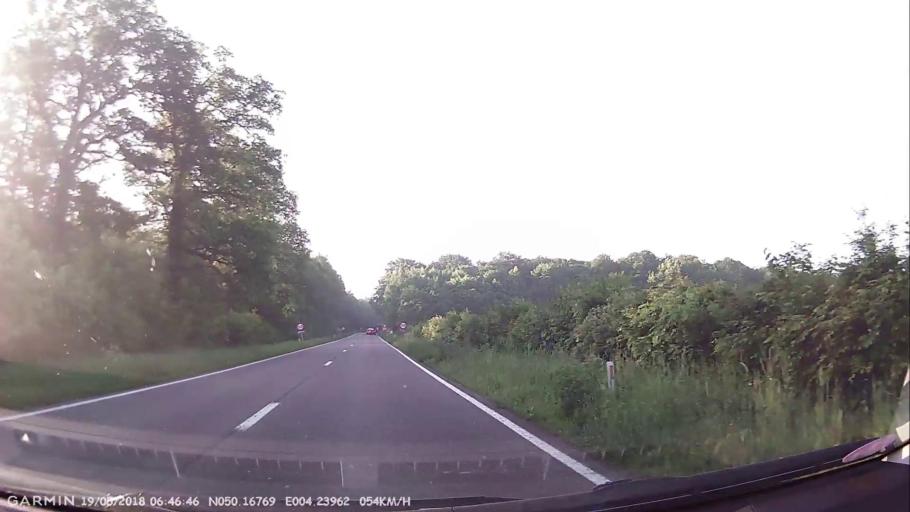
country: BE
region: Wallonia
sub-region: Province du Hainaut
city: Beaumont
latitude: 50.1675
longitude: 4.2399
